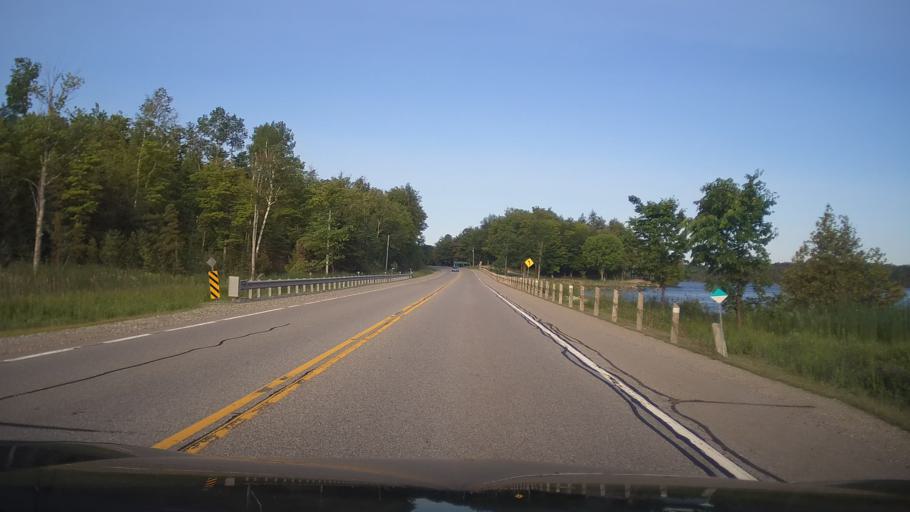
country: CA
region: Ontario
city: Perth
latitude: 44.8255
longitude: -76.5947
